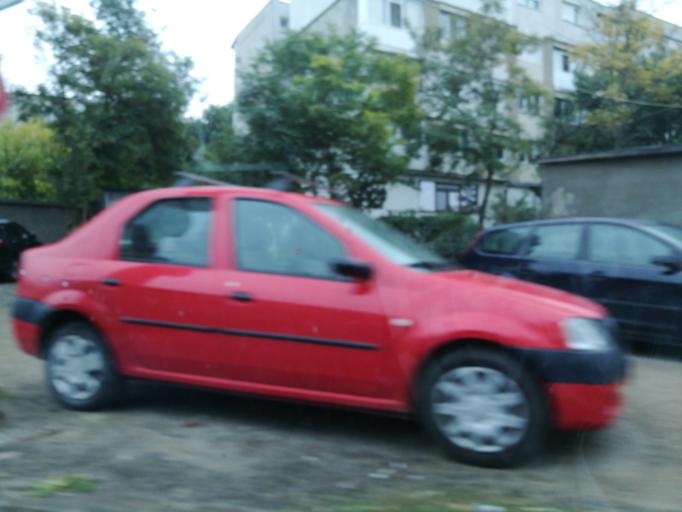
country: RO
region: Galati
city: Galati
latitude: 45.4503
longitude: 28.0162
